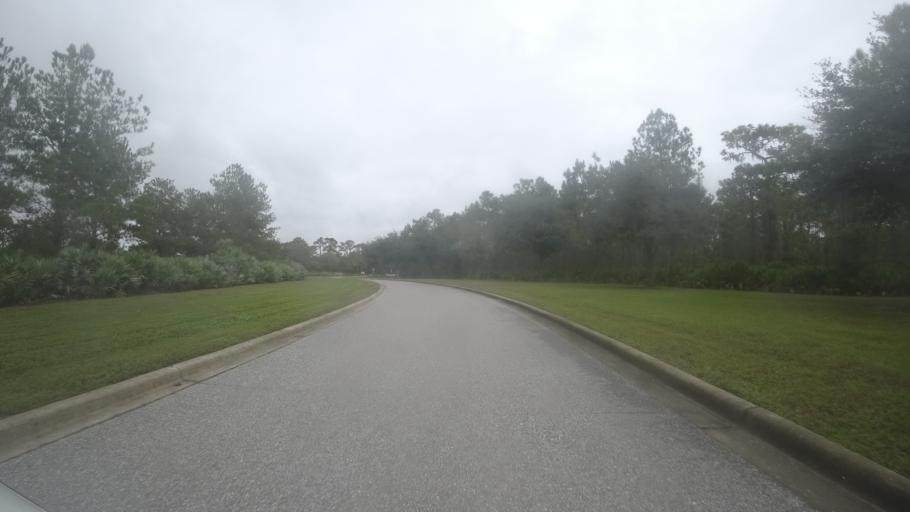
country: US
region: Florida
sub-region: Sarasota County
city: The Meadows
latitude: 27.4097
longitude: -82.3403
